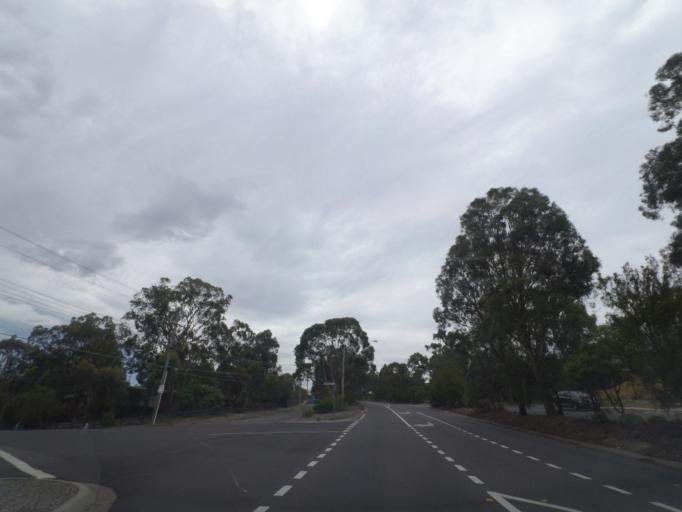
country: AU
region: Victoria
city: Saint Helena
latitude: -37.6975
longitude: 145.1240
